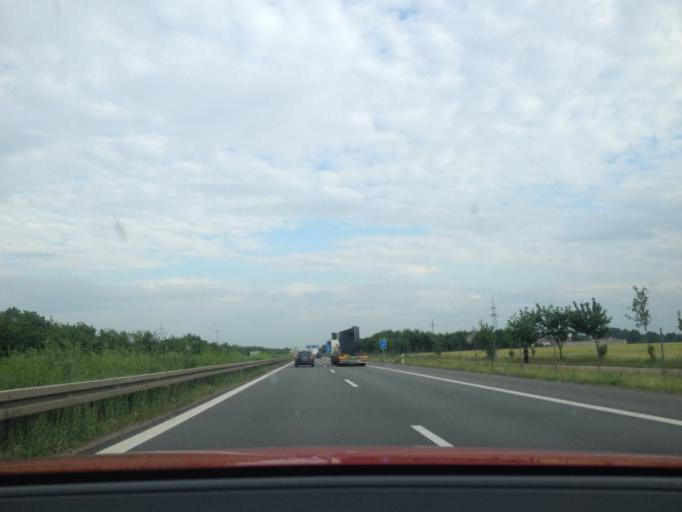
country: DE
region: Saxony-Anhalt
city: Braschwitz
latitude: 51.5175
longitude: 12.0302
